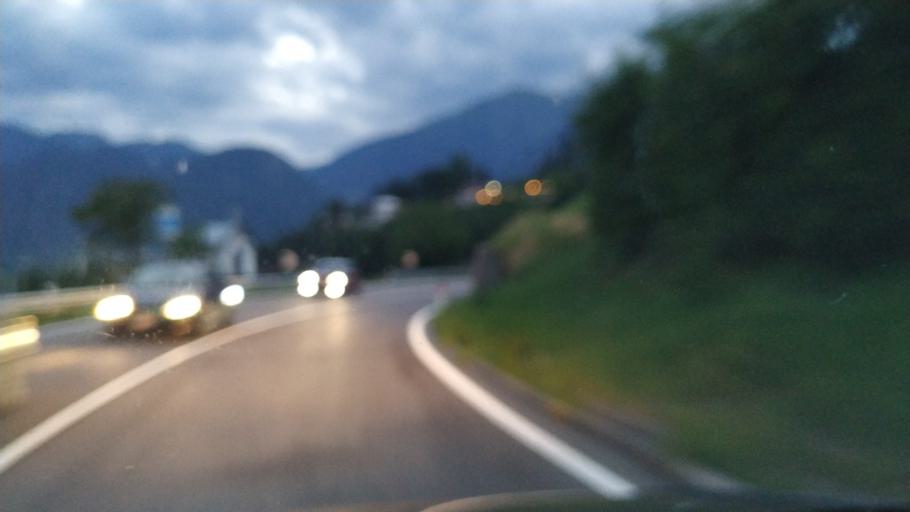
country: IT
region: Trentino-Alto Adige
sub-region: Provincia di Trento
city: Revo
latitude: 46.3914
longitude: 11.0506
